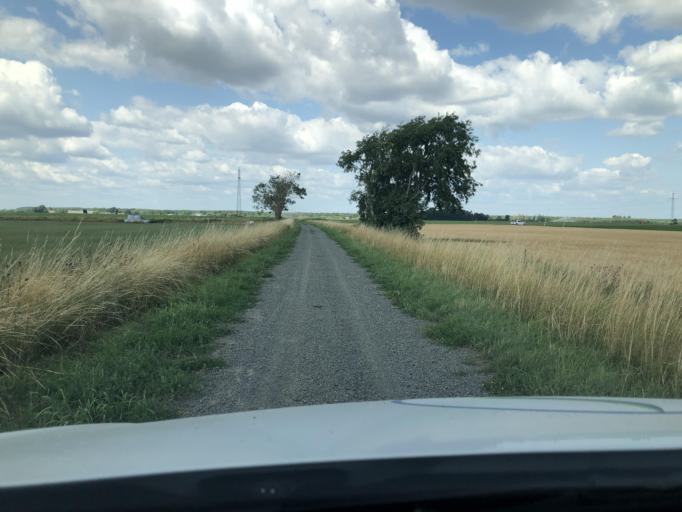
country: SE
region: Skane
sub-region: Kristianstads Kommun
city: Degeberga
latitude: 55.8821
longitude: 14.0818
